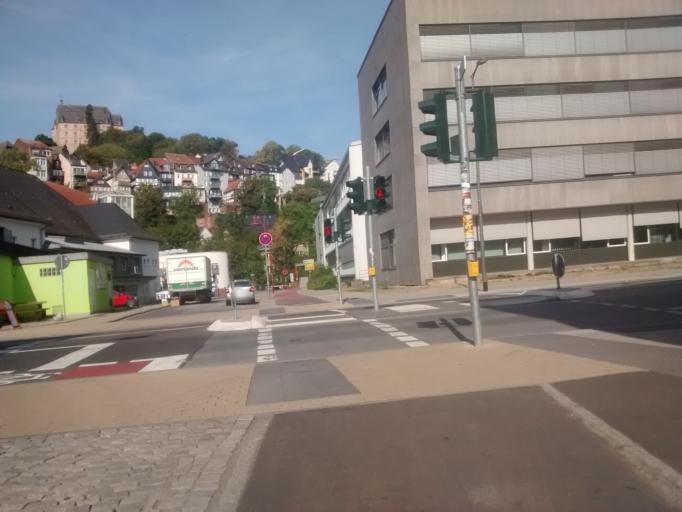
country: DE
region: Hesse
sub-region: Regierungsbezirk Giessen
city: Marburg an der Lahn
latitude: 50.8098
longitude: 8.7744
